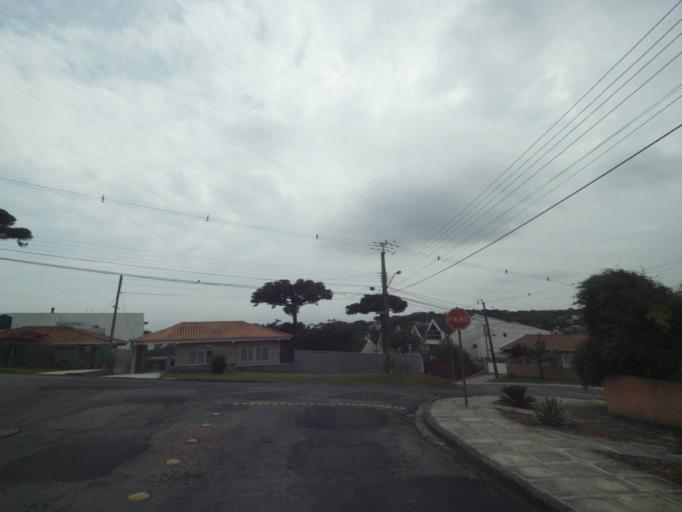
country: BR
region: Parana
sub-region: Curitiba
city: Curitiba
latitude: -25.4004
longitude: -49.3014
